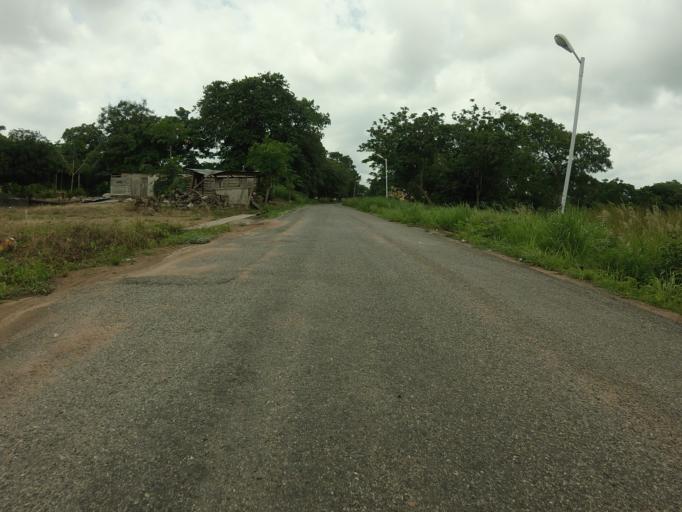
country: GH
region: Volta
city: Ho
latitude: 6.5897
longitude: 0.4644
